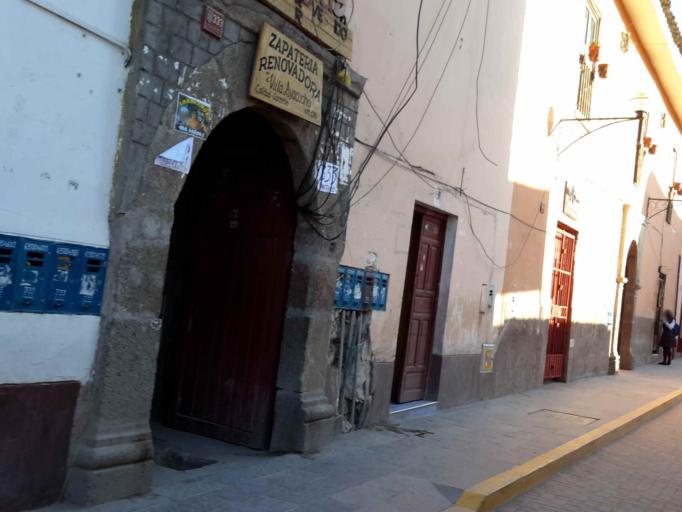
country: PE
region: Ayacucho
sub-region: Provincia de Huamanga
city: Ayacucho
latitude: -13.1570
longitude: -74.2256
